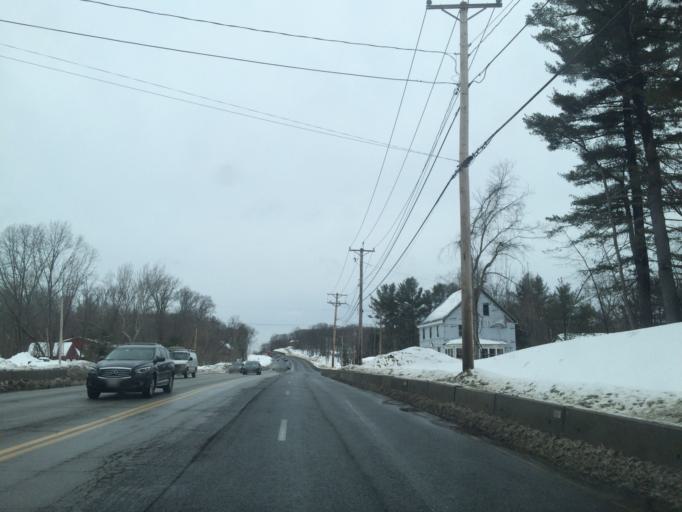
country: US
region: Massachusetts
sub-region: Middlesex County
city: Lincoln
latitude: 42.4447
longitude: -71.3066
